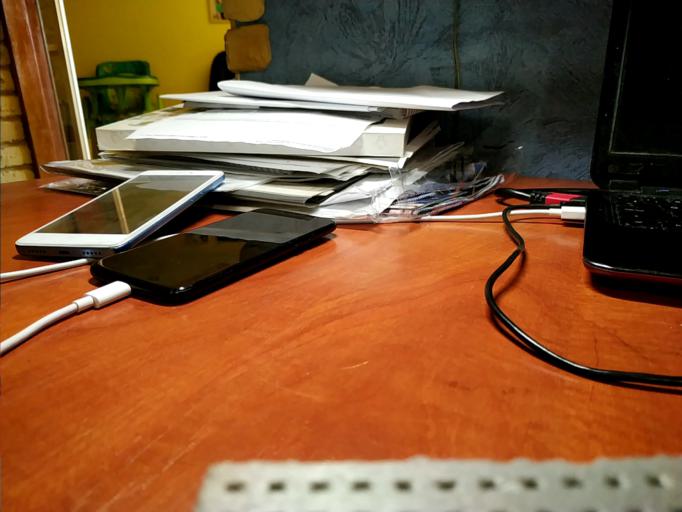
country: RU
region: Tverskaya
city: Kalashnikovo
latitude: 57.4080
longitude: 35.1845
